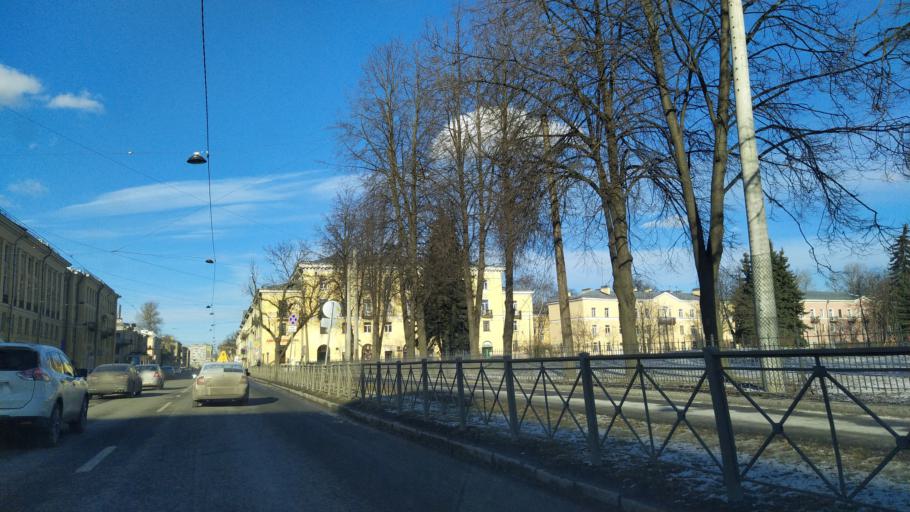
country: RU
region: Leningrad
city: Finlyandskiy
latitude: 59.9479
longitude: 30.4145
